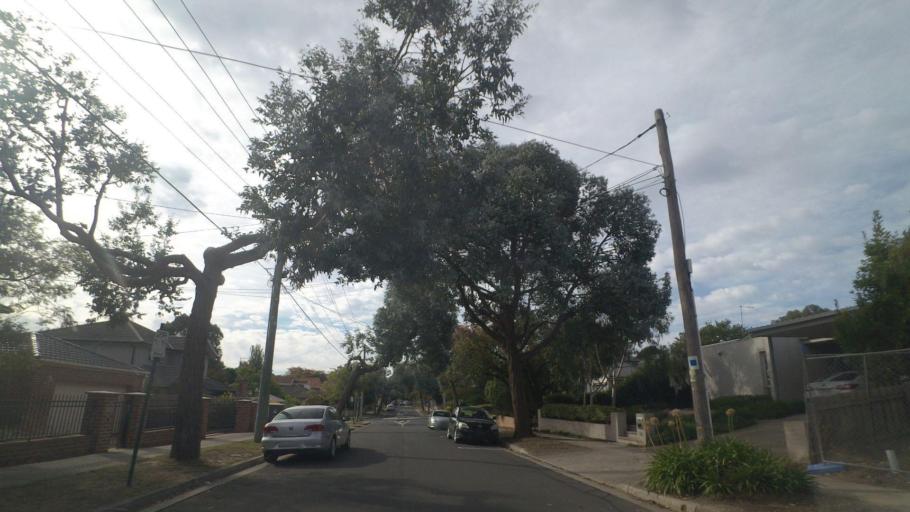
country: AU
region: Victoria
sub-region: Whitehorse
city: Blackburn
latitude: -37.8235
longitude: 145.1418
